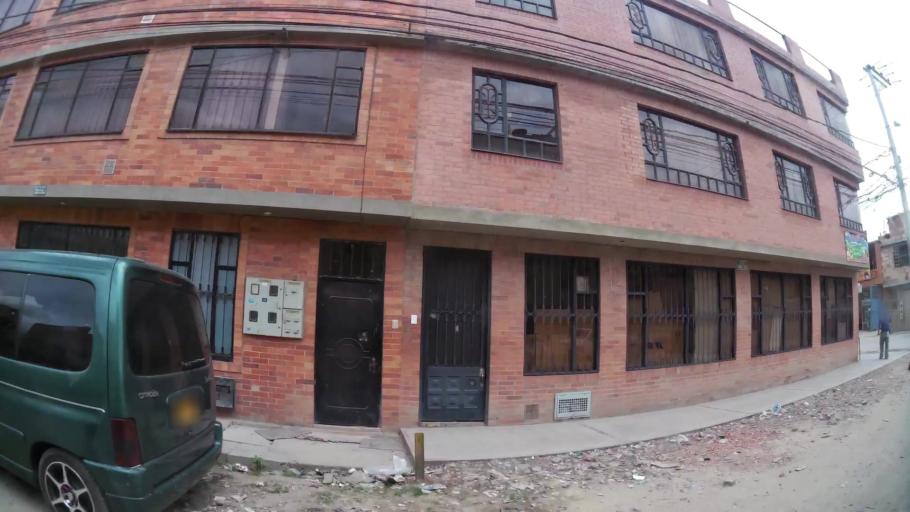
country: CO
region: Cundinamarca
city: Funza
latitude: 4.7196
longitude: -74.1315
